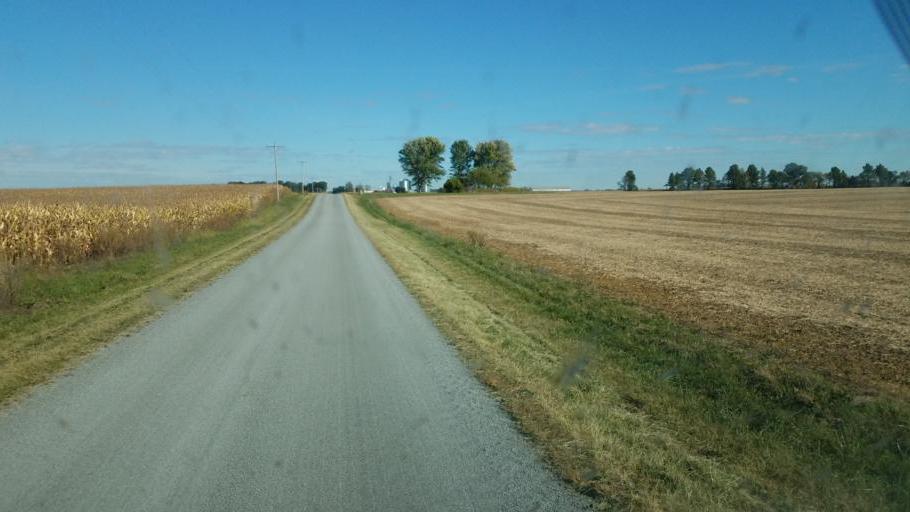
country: US
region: Ohio
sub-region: Marion County
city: Marion
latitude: 40.7044
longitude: -83.2073
